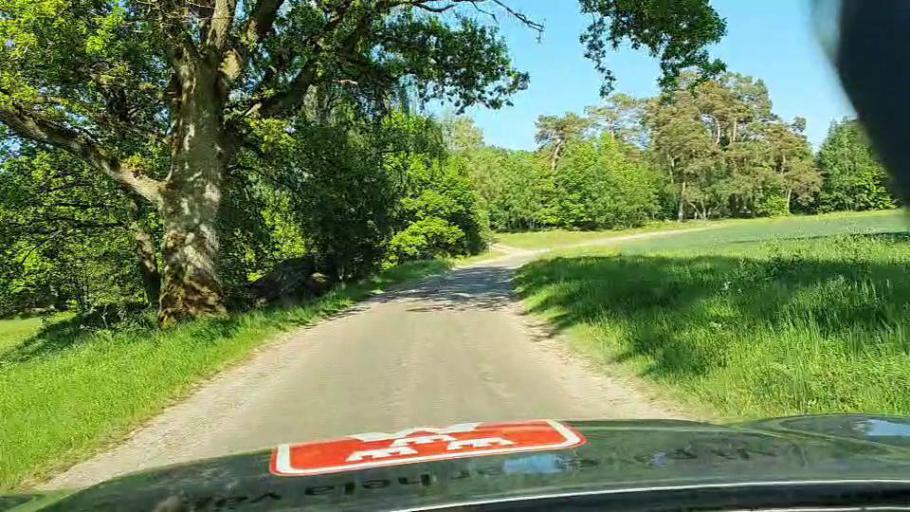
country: SE
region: Skane
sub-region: Hassleholms Kommun
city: Tormestorp
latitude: 56.1168
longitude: 13.7160
